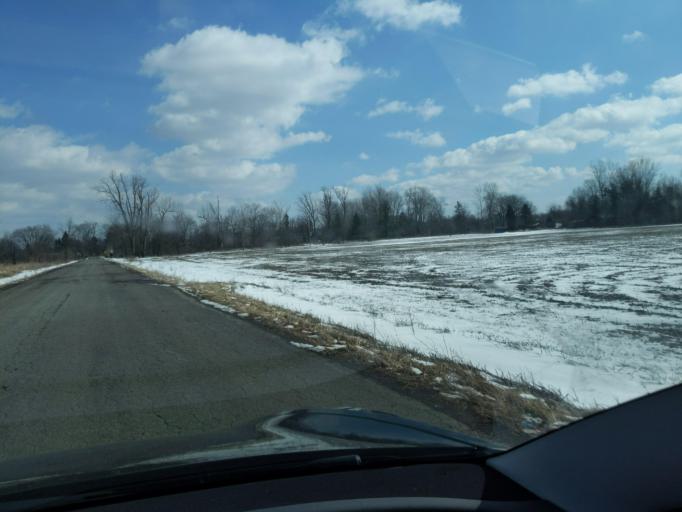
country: US
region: Michigan
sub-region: Ingham County
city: Webberville
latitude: 42.6142
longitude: -84.1508
